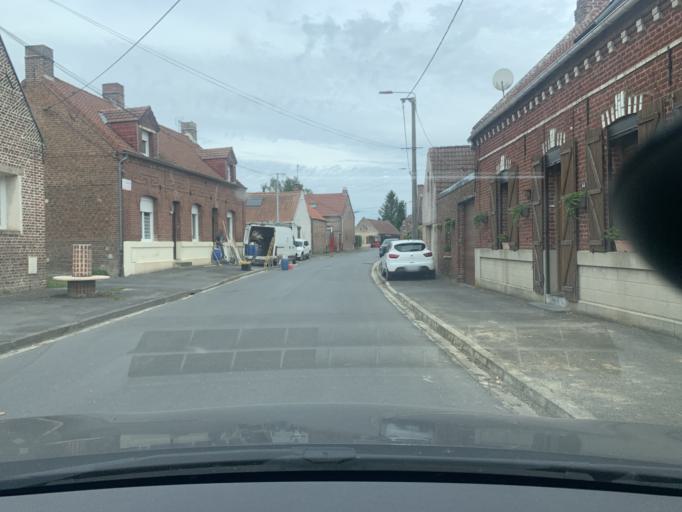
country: FR
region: Nord-Pas-de-Calais
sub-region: Departement du Nord
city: Marcoing
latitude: 50.1402
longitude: 3.1797
